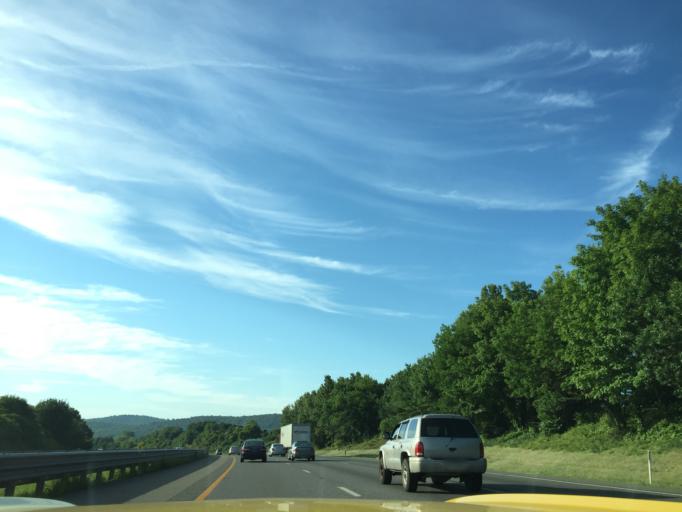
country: US
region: New Jersey
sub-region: Warren County
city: Alpha
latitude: 40.6551
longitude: -75.1706
